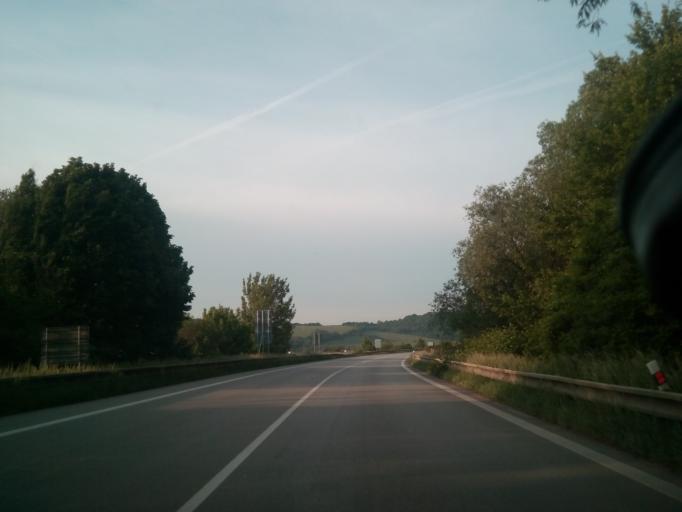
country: SK
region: Kosicky
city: Roznava
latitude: 48.5443
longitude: 20.3969
